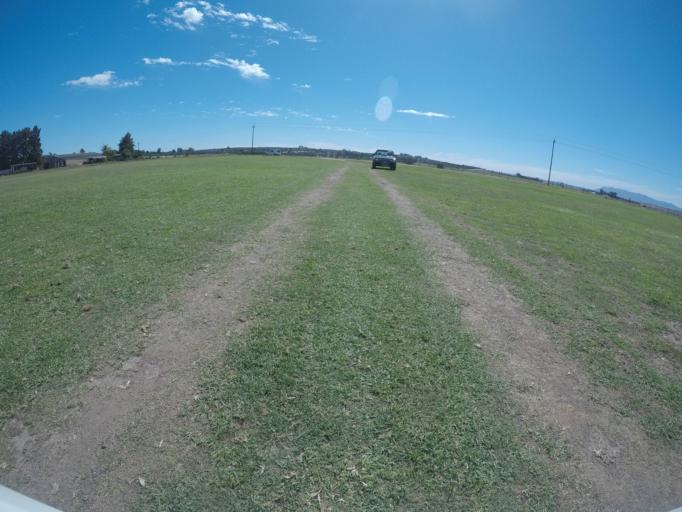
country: ZA
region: Western Cape
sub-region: West Coast District Municipality
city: Malmesbury
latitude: -33.5251
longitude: 18.6540
